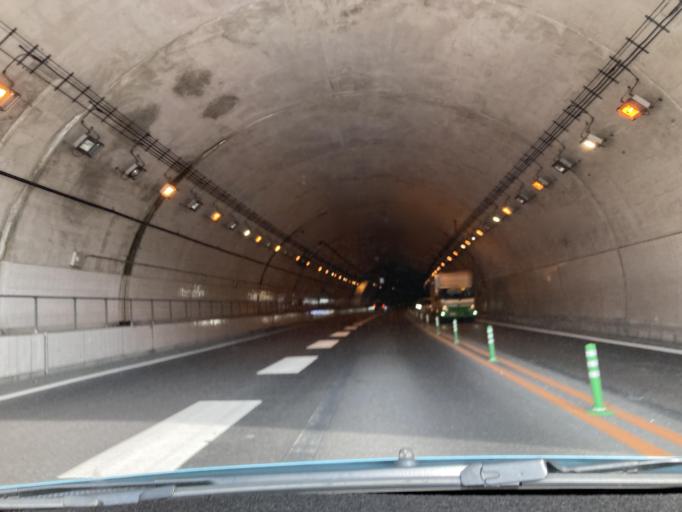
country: JP
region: Okinawa
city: Nago
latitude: 26.5745
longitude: 127.9902
